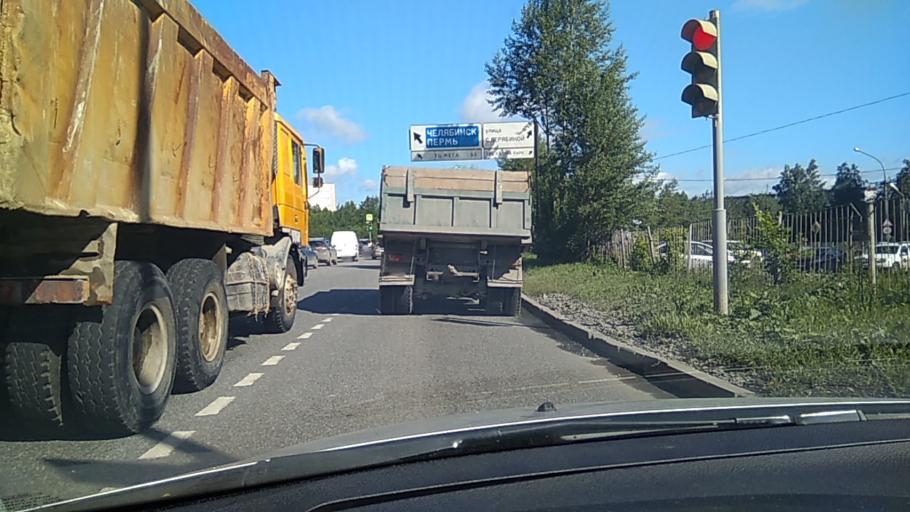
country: RU
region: Sverdlovsk
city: Sovkhoznyy
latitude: 56.8044
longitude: 60.5417
